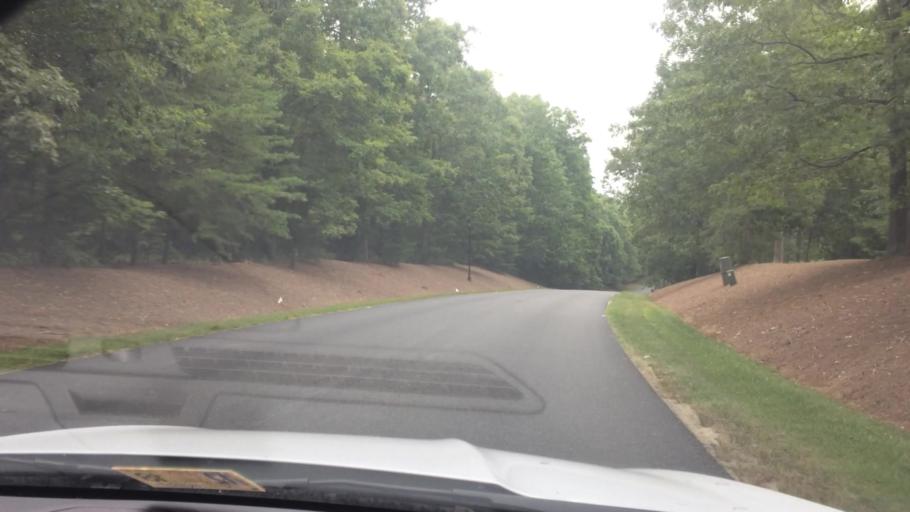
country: US
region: Virginia
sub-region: James City County
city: Williamsburg
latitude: 37.3087
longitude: -76.7942
